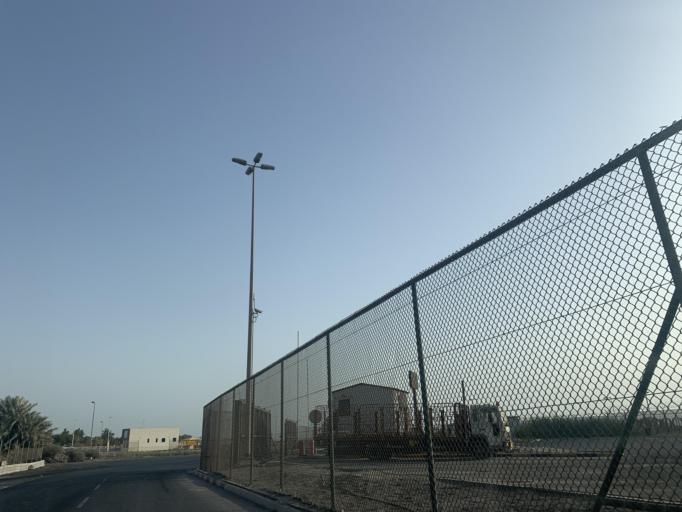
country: BH
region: Central Governorate
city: Madinat Hamad
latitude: 26.1737
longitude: 50.4523
